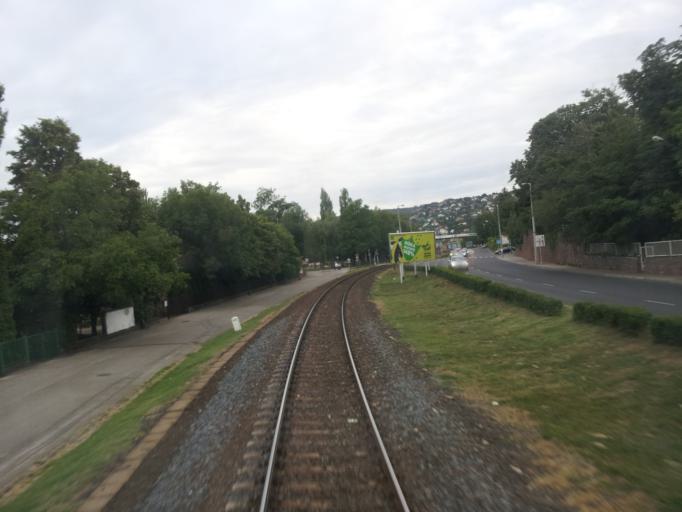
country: HU
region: Veszprem
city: Balatonalmadi
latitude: 47.0293
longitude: 18.0238
